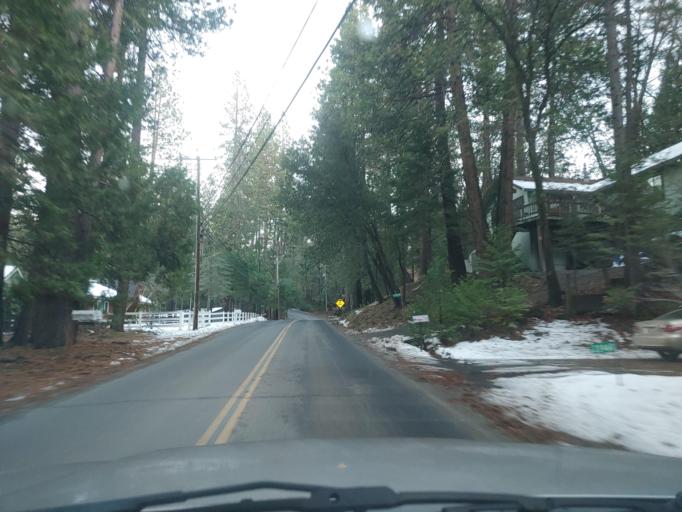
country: US
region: California
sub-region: Tuolumne County
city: Twain Harte
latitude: 38.0305
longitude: -120.2632
